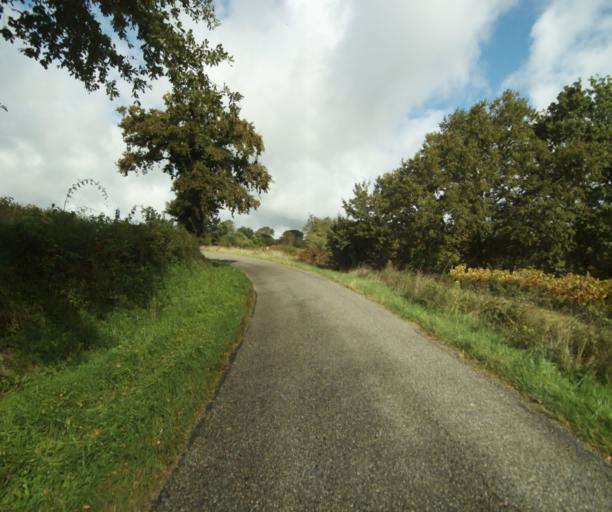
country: FR
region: Midi-Pyrenees
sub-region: Departement du Gers
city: Nogaro
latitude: 43.8307
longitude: -0.0971
